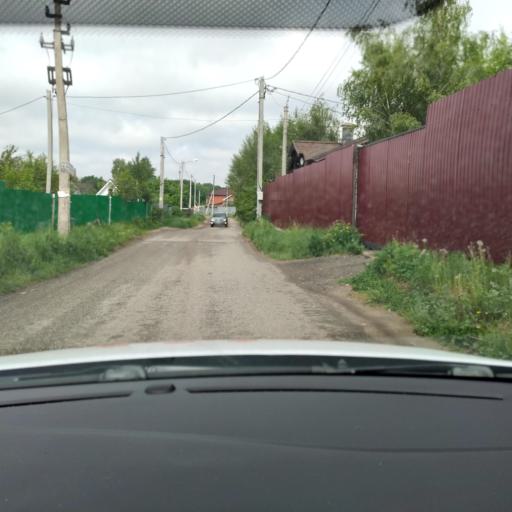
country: RU
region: Tatarstan
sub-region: Gorod Kazan'
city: Kazan
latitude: 55.8223
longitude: 49.2236
